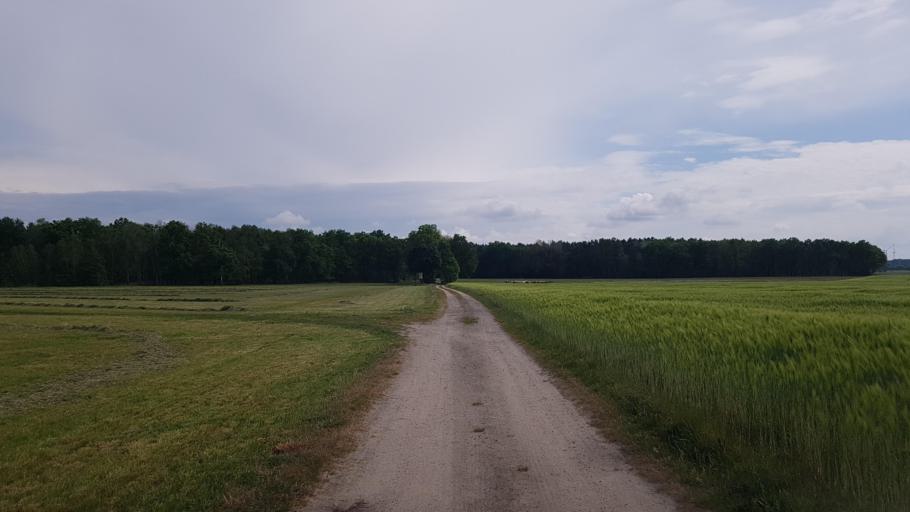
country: DE
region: Brandenburg
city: Sallgast
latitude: 51.5995
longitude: 13.8662
